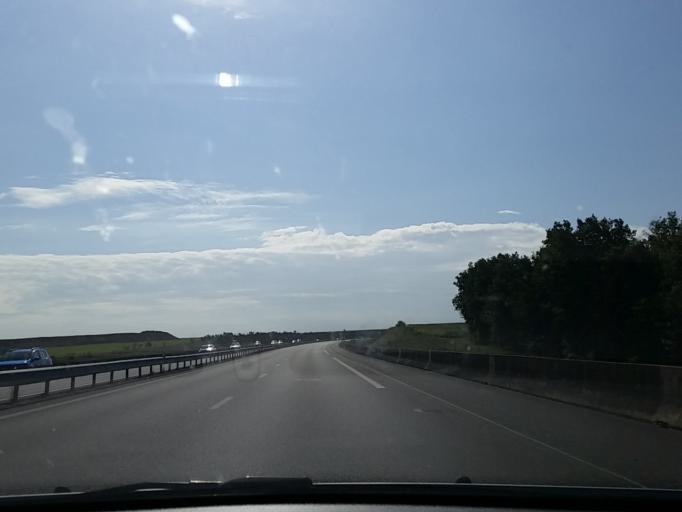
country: FR
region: Centre
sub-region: Departement du Cher
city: Trouy
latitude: 47.0064
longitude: 2.3938
